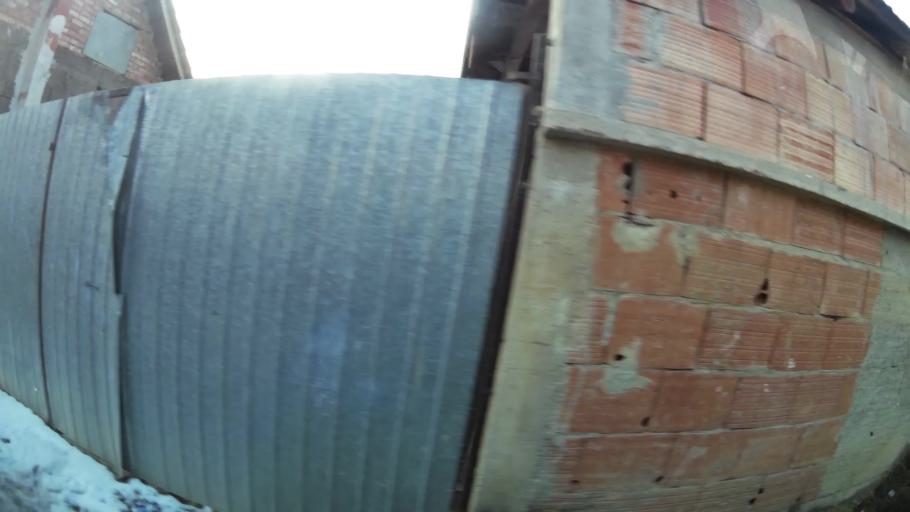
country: MK
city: Creshevo
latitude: 42.0165
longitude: 21.5207
